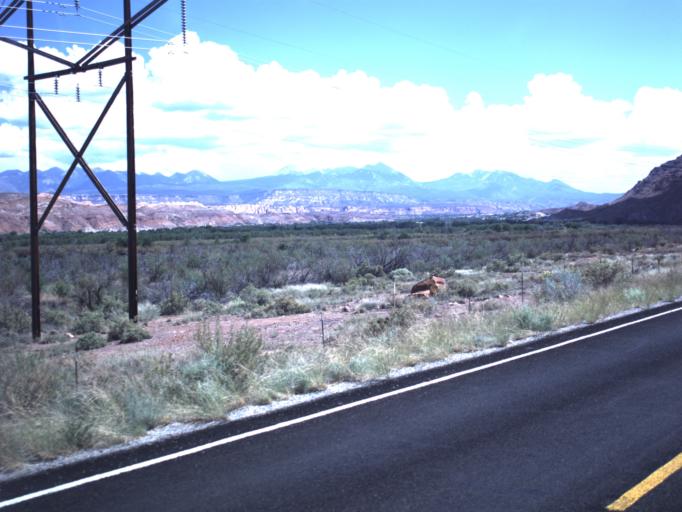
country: US
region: Utah
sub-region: Grand County
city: Moab
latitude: 38.5883
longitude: -109.5930
